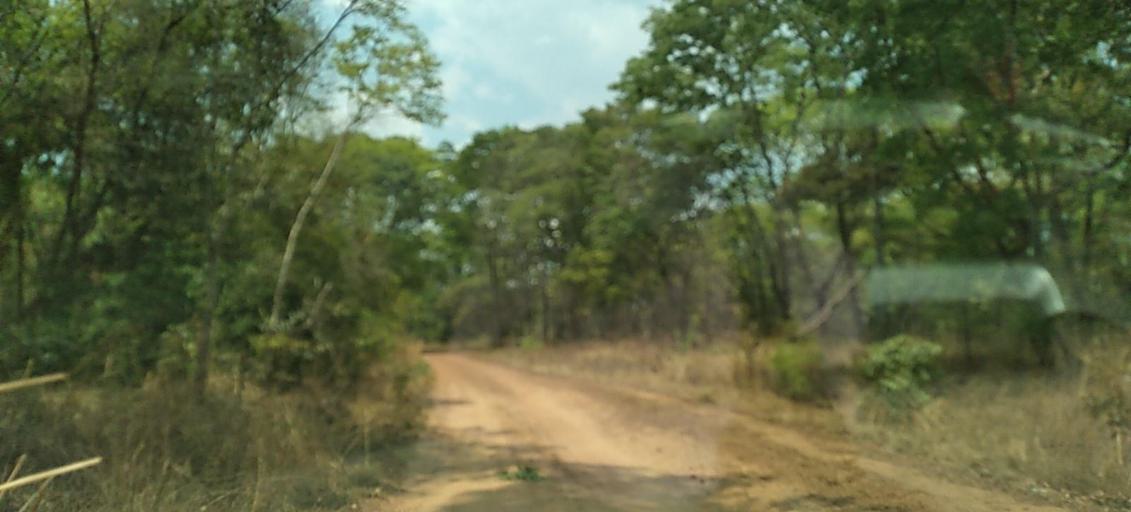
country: ZM
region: Copperbelt
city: Chingola
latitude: -12.7830
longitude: 27.6667
